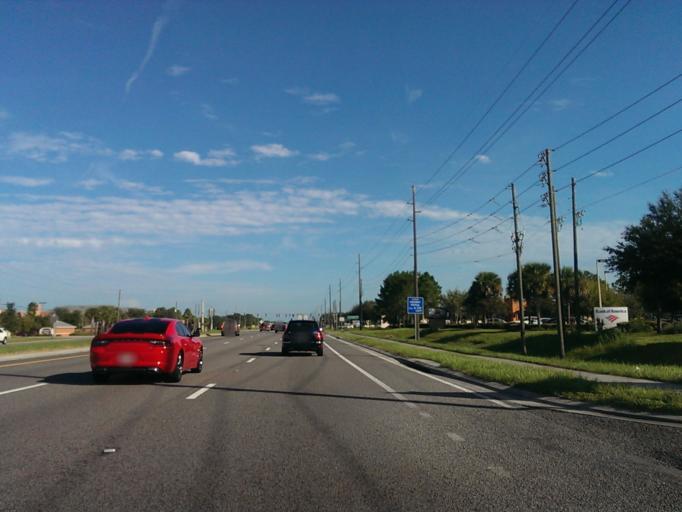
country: US
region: Florida
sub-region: Lake County
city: Four Corners
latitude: 28.3524
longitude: -81.6757
